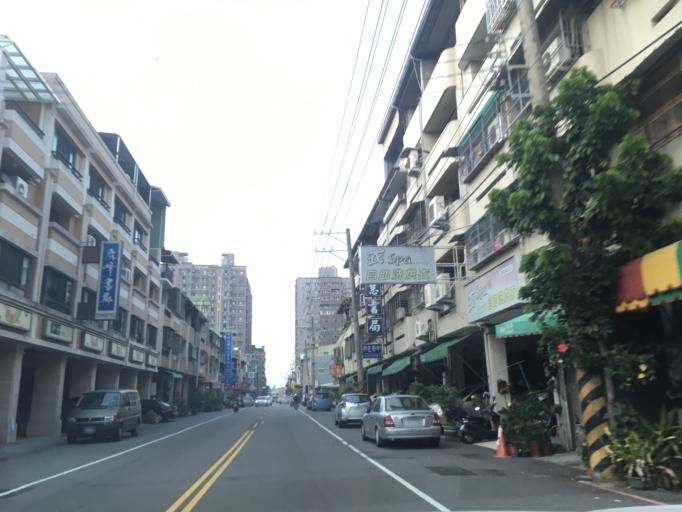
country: TW
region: Taiwan
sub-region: Taichung City
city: Taichung
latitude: 24.1813
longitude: 120.6951
